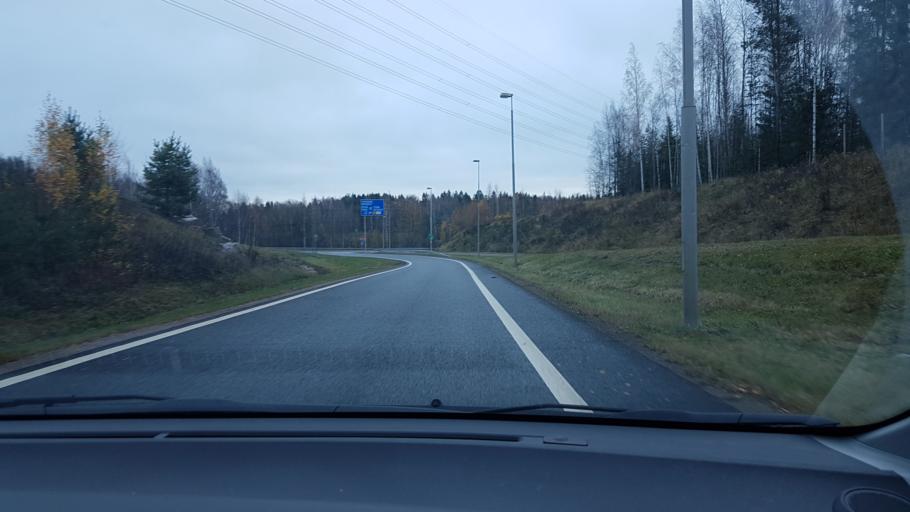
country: FI
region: Uusimaa
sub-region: Helsinki
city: Vantaa
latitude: 60.2559
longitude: 25.1257
